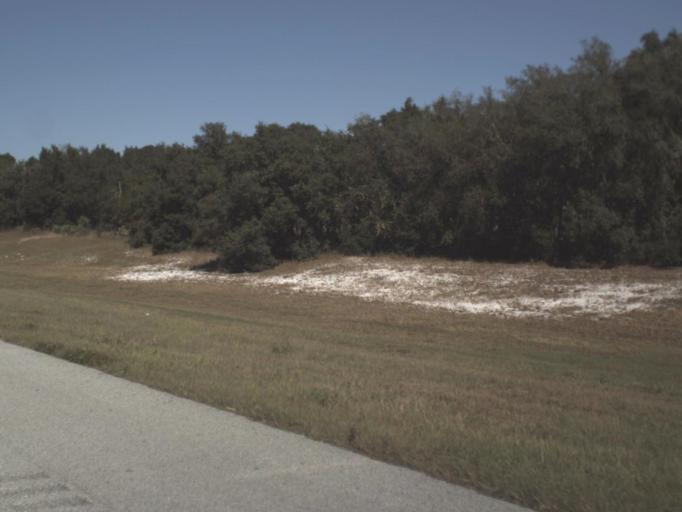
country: US
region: Florida
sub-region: Lake County
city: Hawthorne
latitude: 28.7240
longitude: -81.9055
